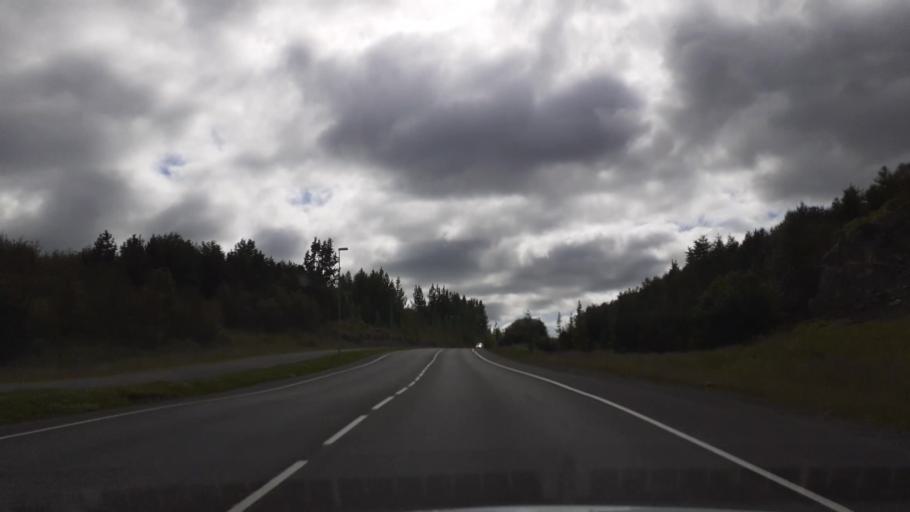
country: IS
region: Northeast
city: Akureyri
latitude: 65.6838
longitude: -18.1157
